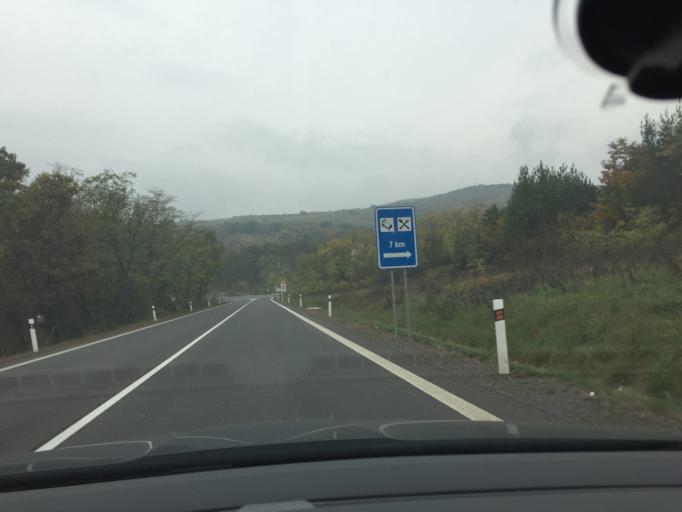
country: SK
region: Banskobystricky
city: Velky Krtis
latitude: 48.2240
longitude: 19.3774
